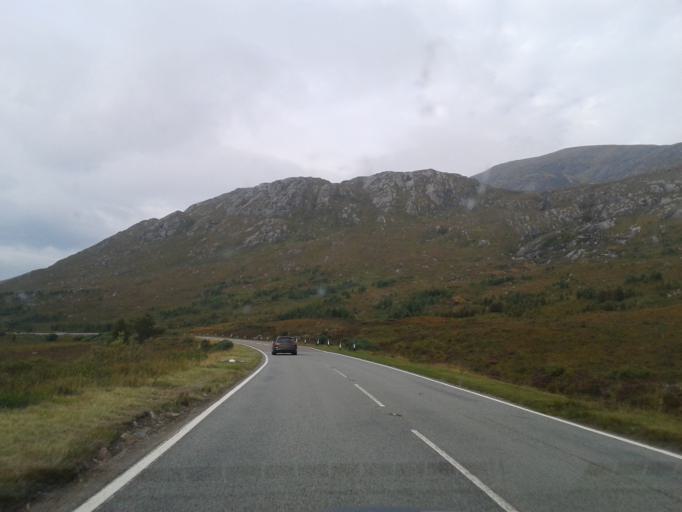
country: GB
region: Scotland
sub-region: Highland
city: Spean Bridge
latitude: 57.1501
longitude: -5.0369
